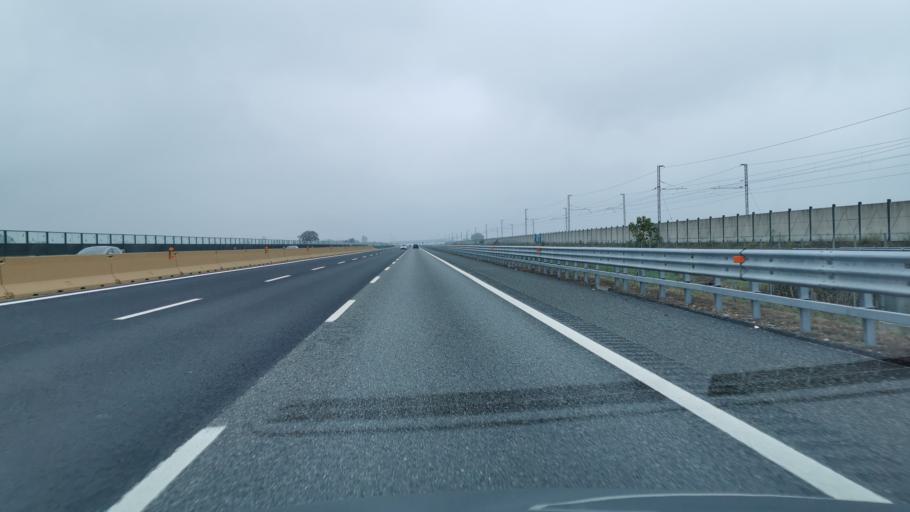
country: IT
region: Piedmont
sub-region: Provincia di Vercelli
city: Saluggia
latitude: 45.2659
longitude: 8.0131
